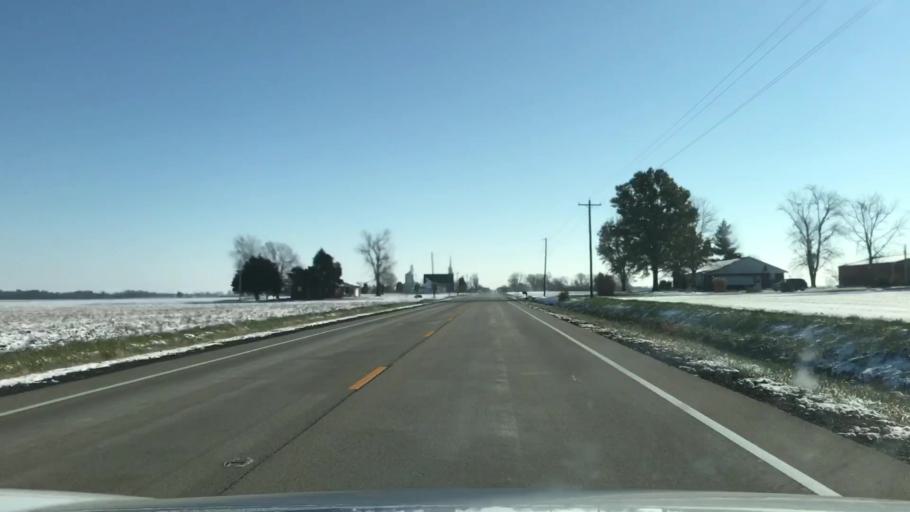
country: US
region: Illinois
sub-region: Washington County
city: Okawville
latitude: 38.4423
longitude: -89.4979
